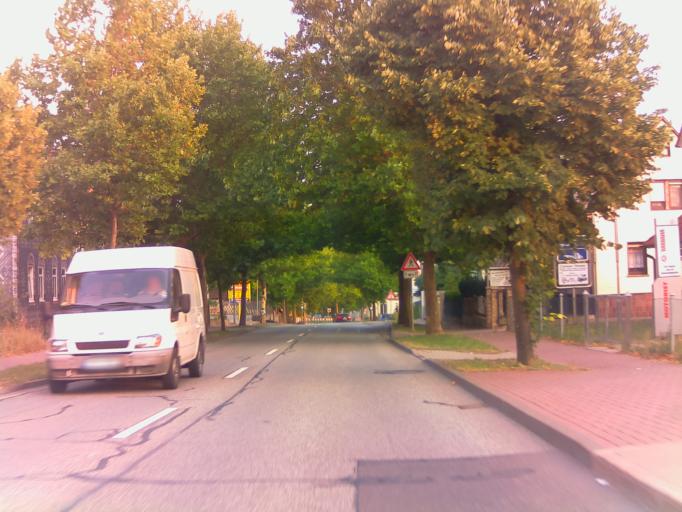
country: DE
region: Thuringia
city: Bad Berka
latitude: 50.9036
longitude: 11.2792
